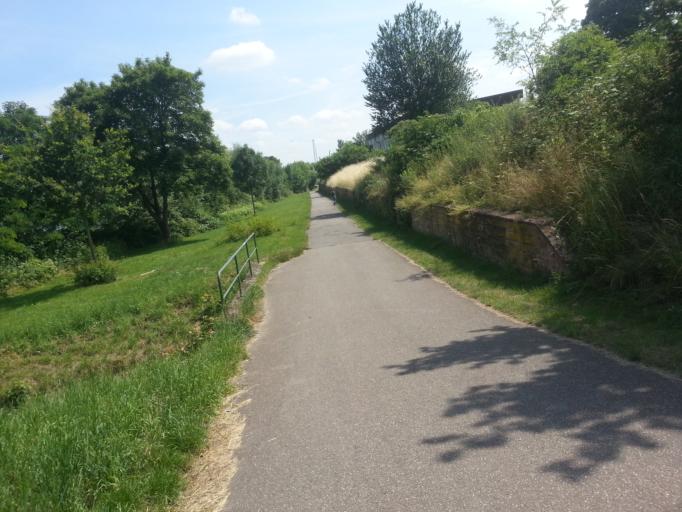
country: DE
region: Baden-Wuerttemberg
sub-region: Karlsruhe Region
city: Edingen-Neckarhausen
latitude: 49.4655
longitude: 8.6032
